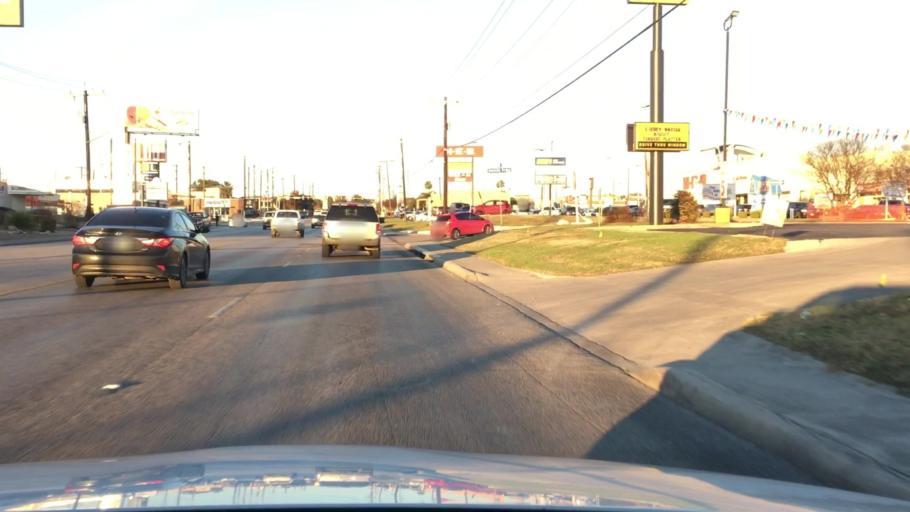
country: US
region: Texas
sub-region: Bexar County
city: Windcrest
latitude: 29.5483
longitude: -98.4088
